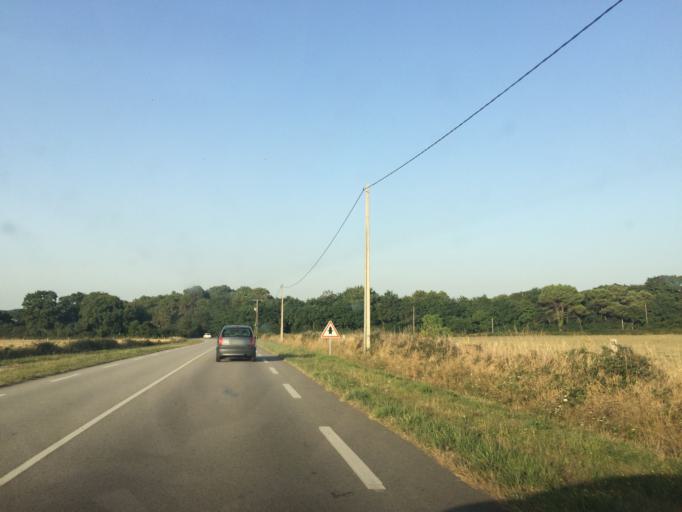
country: FR
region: Brittany
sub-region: Departement du Morbihan
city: Ambon
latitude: 47.5442
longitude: -2.5285
